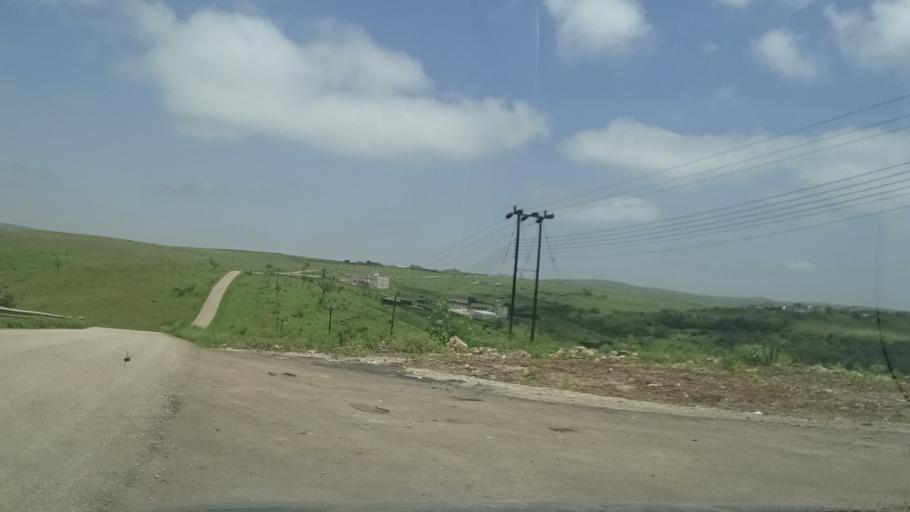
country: OM
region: Zufar
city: Salalah
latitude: 17.2211
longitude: 54.2034
